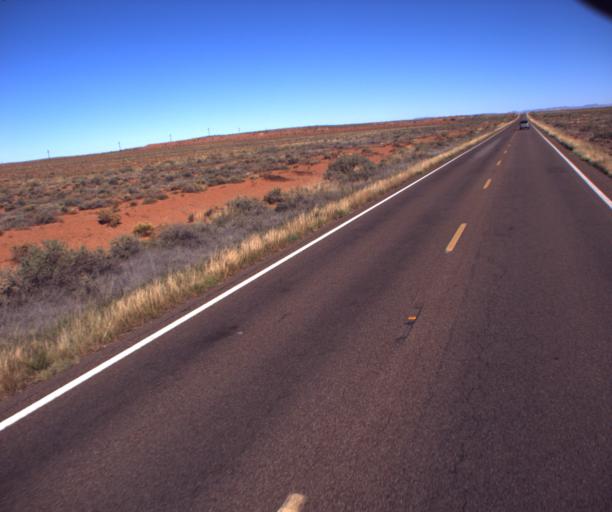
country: US
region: Arizona
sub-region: Navajo County
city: Holbrook
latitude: 34.8177
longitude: -110.1399
